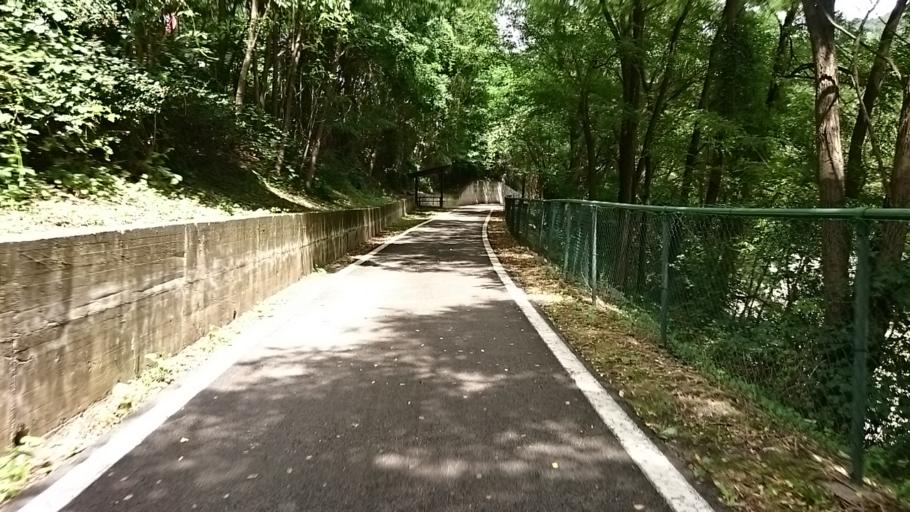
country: IT
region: Trentino-Alto Adige
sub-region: Bolzano
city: Villandro
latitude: 46.6202
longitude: 11.5401
